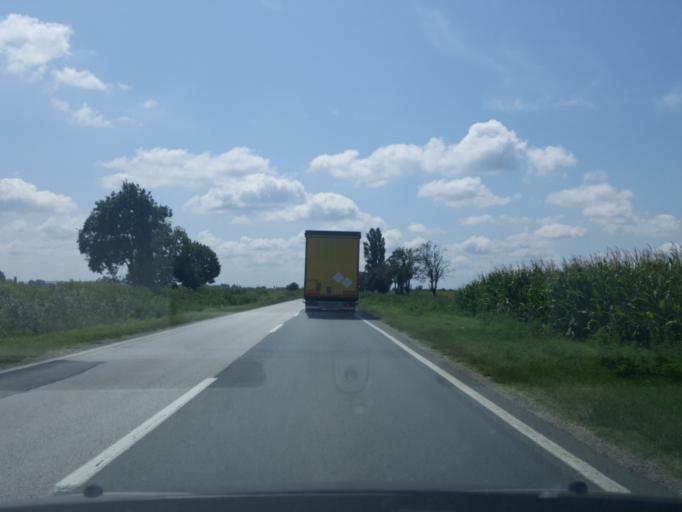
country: RS
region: Autonomna Pokrajina Vojvodina
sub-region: Sremski Okrug
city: Sremska Mitrovica
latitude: 44.9906
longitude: 19.6407
